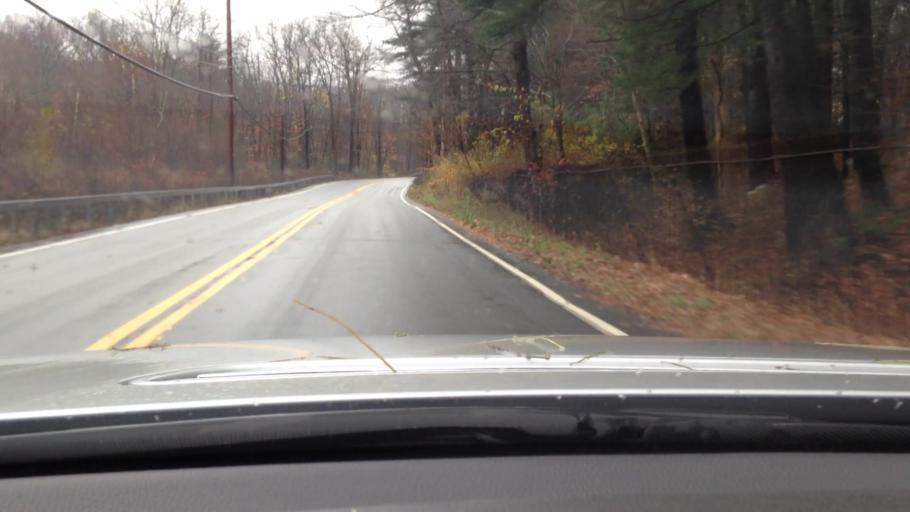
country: US
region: New York
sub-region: Orange County
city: West Point
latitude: 41.3974
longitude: -73.9333
